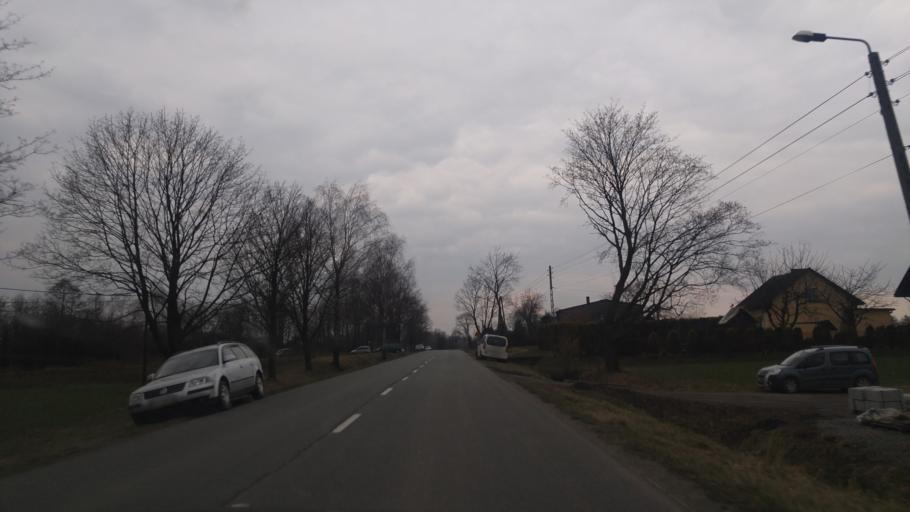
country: PL
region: Silesian Voivodeship
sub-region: Powiat cieszynski
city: Strumien
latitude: 49.9282
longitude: 18.7892
